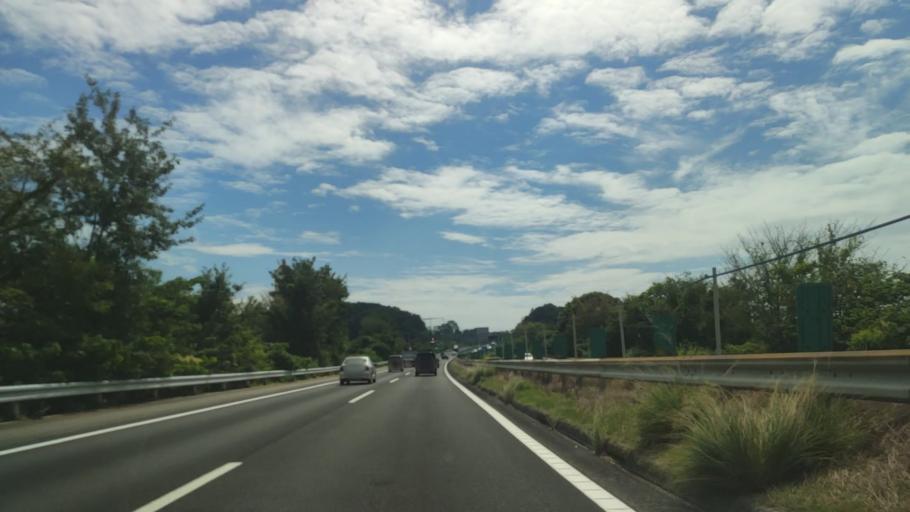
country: JP
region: Aichi
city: Okazaki
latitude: 34.9907
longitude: 137.1845
